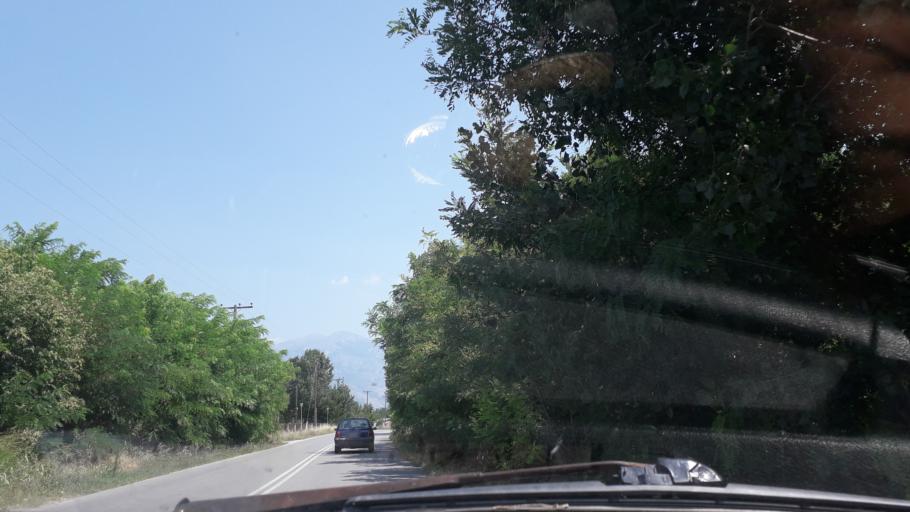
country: GR
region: Central Macedonia
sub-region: Nomos Pellis
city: Aridaia
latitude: 40.9631
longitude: 22.0512
